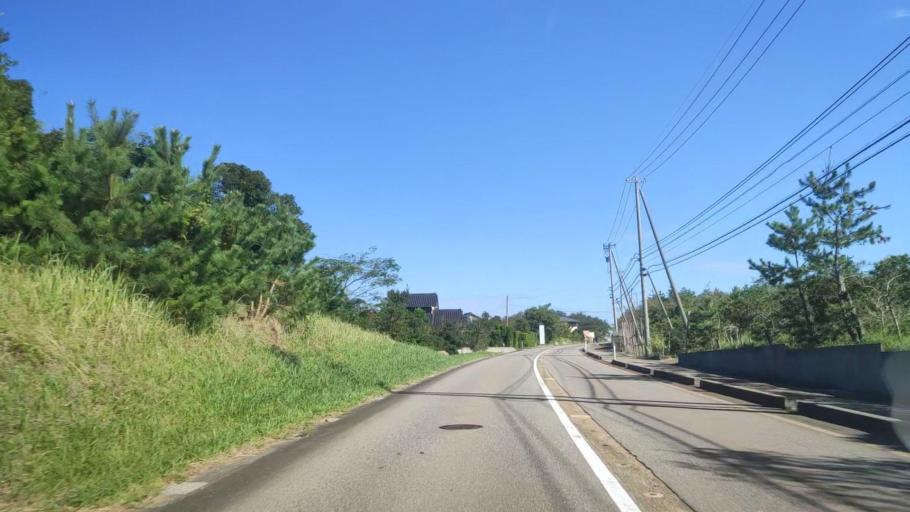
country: JP
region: Ishikawa
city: Hakui
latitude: 36.9852
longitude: 136.7757
